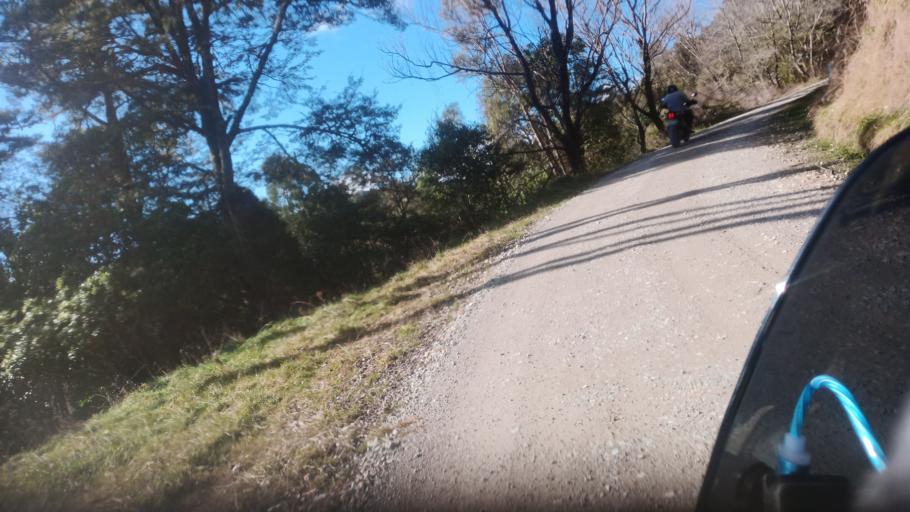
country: NZ
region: Hawke's Bay
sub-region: Wairoa District
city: Wairoa
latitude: -38.6631
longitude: 177.5129
